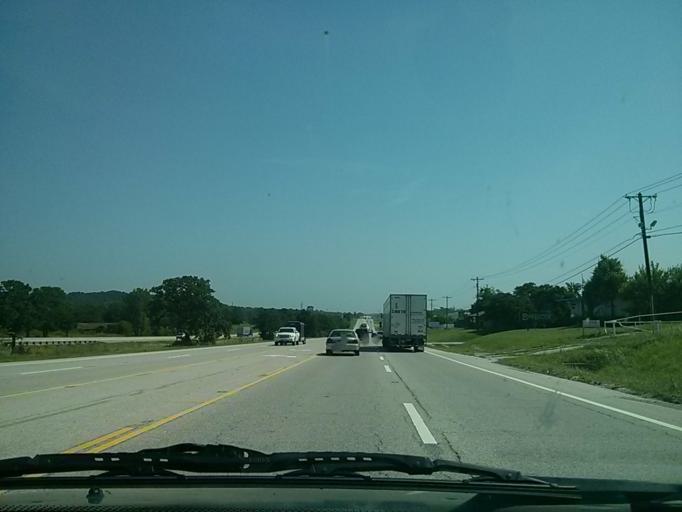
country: US
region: Oklahoma
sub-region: Tulsa County
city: Oakhurst
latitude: 36.0382
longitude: -96.0832
